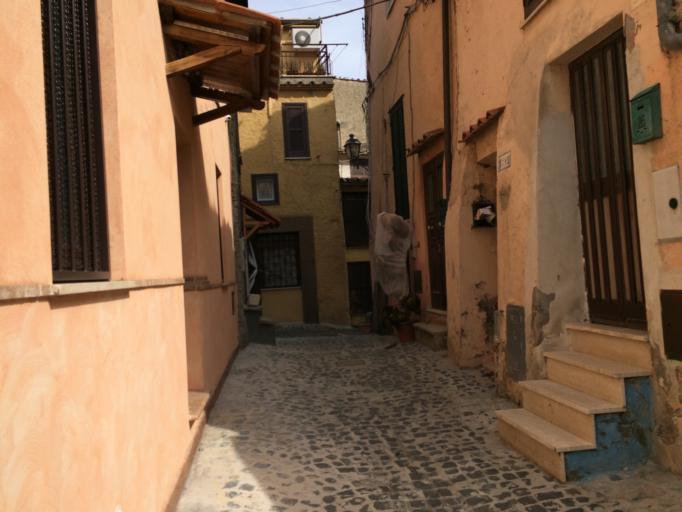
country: IT
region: Latium
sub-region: Citta metropolitana di Roma Capitale
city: Anguillara Sabazia
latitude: 42.0932
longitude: 12.2705
